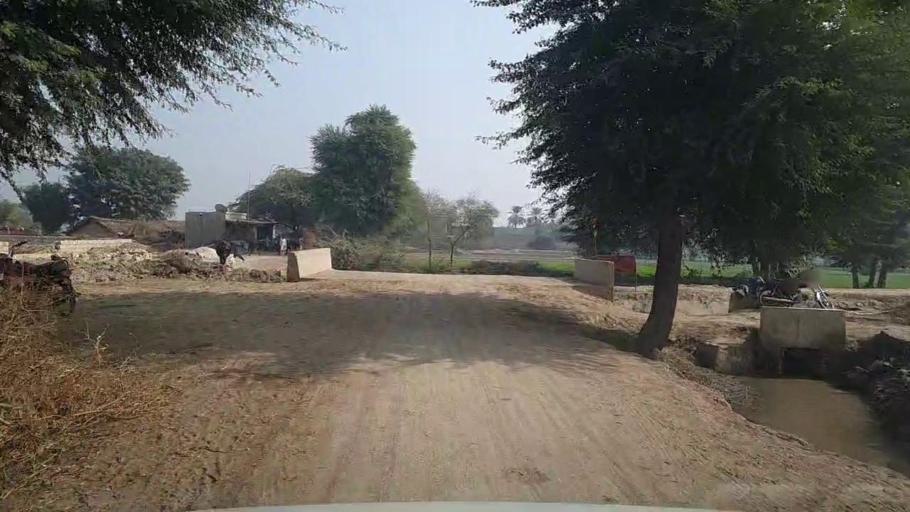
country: PK
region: Sindh
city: Setharja Old
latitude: 27.1408
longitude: 68.4970
